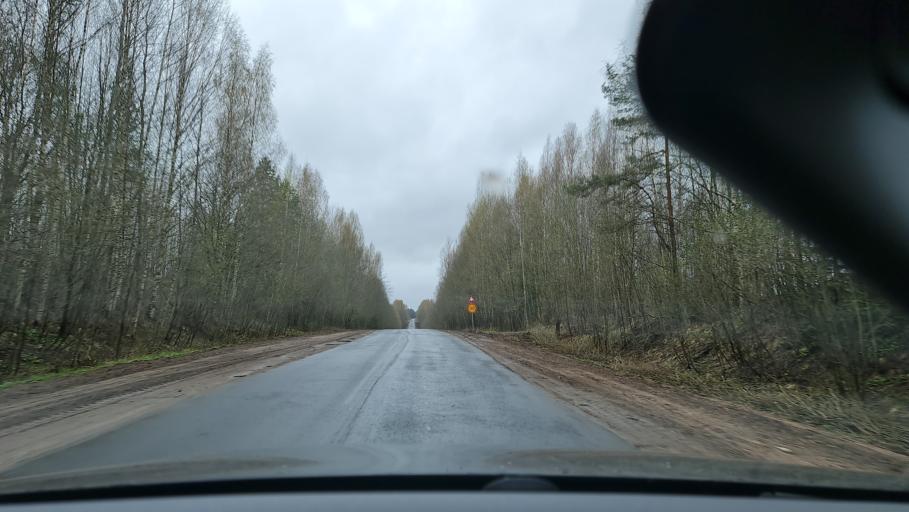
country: RU
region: Novgorod
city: Demyansk
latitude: 57.7388
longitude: 32.5736
